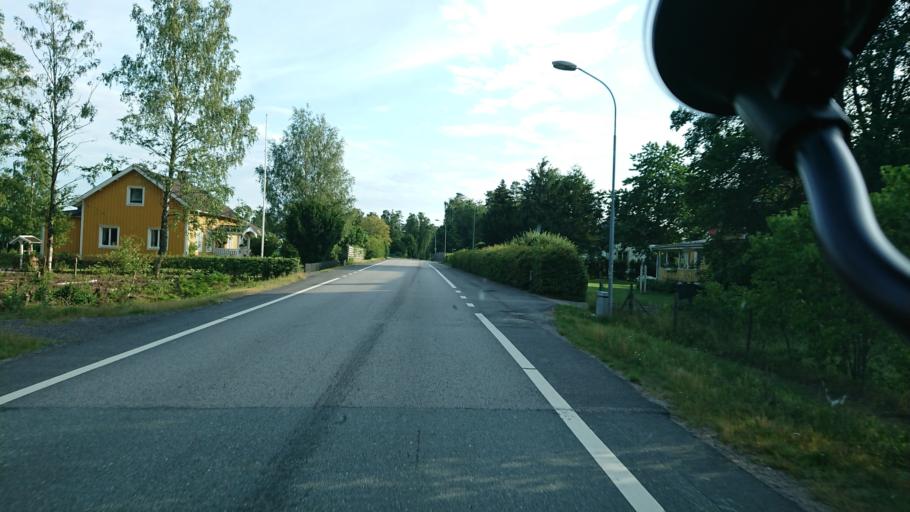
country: SE
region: Kronoberg
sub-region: Vaxjo Kommun
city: Rottne
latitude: 57.0318
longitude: 14.8968
